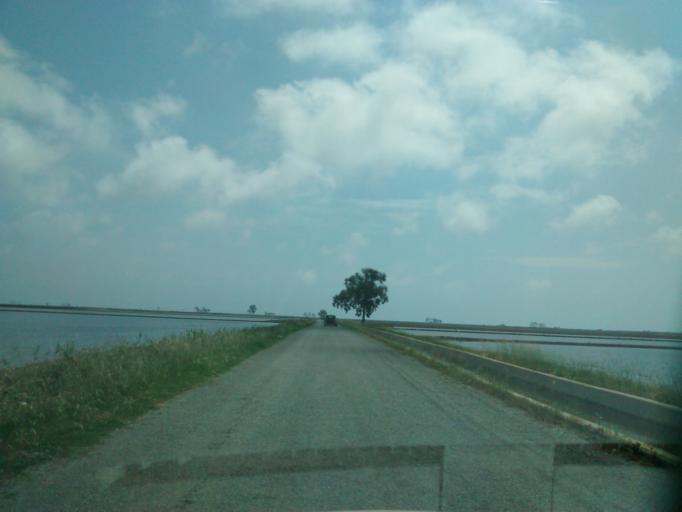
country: ES
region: Catalonia
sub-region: Provincia de Tarragona
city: Deltebre
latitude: 40.6878
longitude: 0.7833
